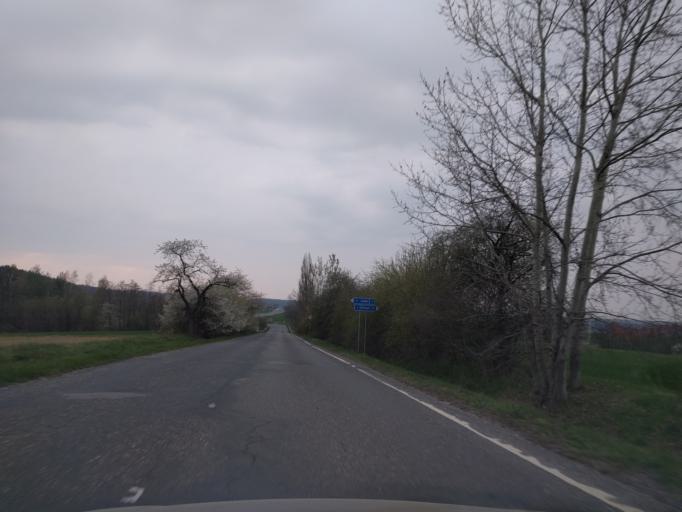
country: CZ
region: Central Bohemia
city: Kostelec nad Cernymi Lesy
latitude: 49.9928
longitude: 14.8357
